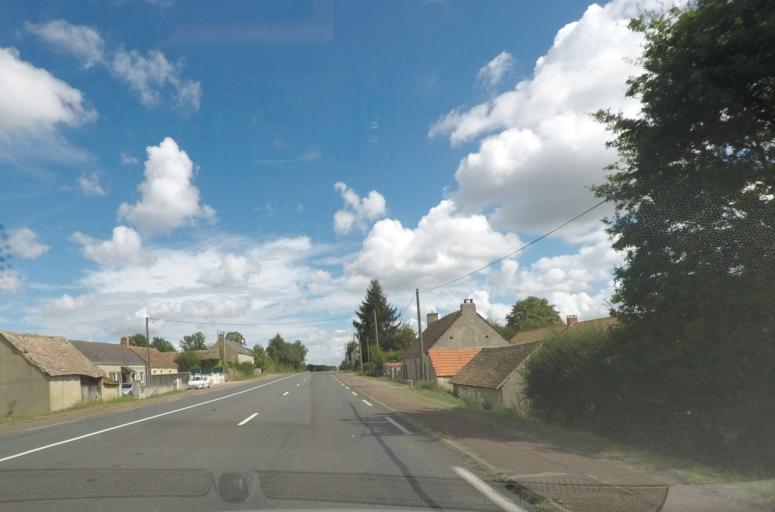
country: FR
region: Pays de la Loire
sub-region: Departement de la Sarthe
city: Cerans-Foulletourte
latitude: 47.7953
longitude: 0.0458
